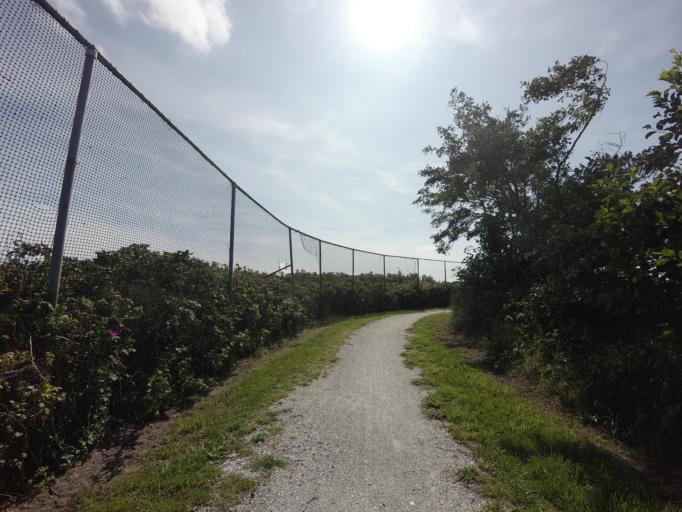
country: NL
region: Friesland
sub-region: Gemeente Ameland
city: Hollum
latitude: 53.4503
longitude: 5.6478
